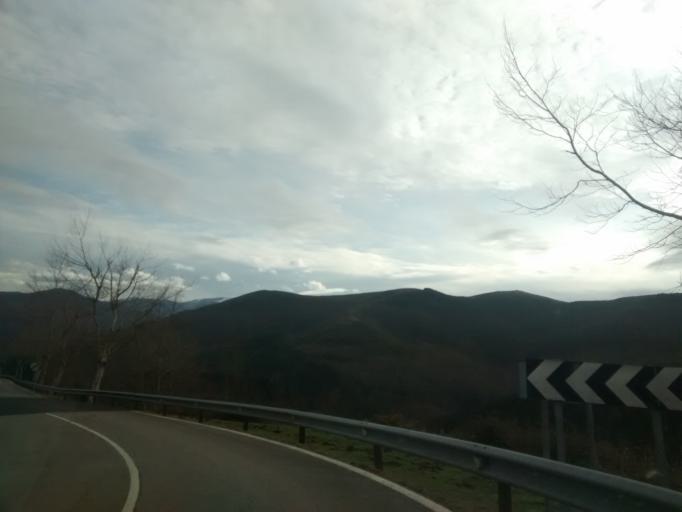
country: ES
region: Cantabria
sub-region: Provincia de Cantabria
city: Ruente
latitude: 43.2363
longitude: -4.3236
